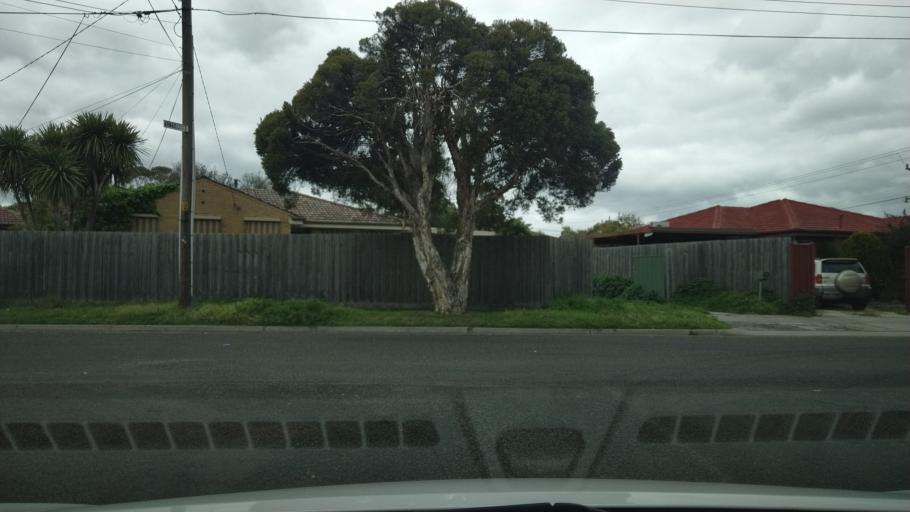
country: AU
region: Victoria
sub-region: Greater Dandenong
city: Keysborough
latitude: -37.9834
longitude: 145.1789
